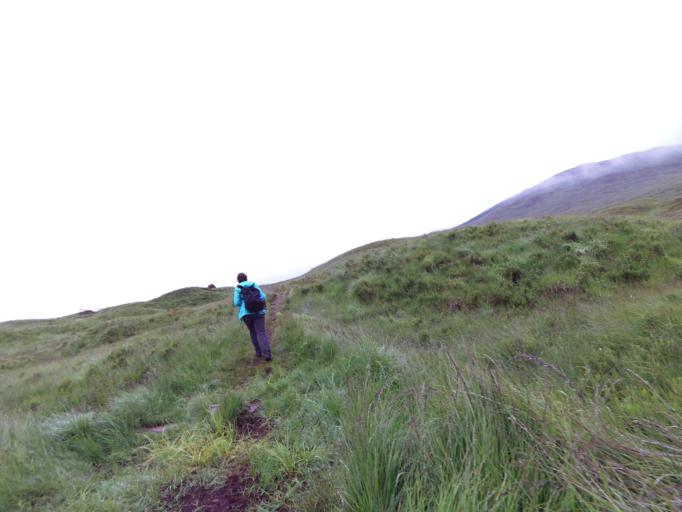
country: GB
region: Scotland
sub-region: Highland
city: Spean Bridge
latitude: 56.7719
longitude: -4.7104
